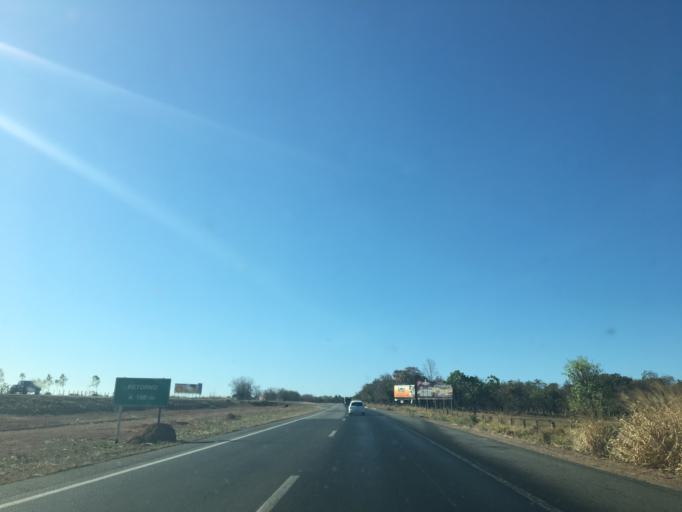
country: BR
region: Goias
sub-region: Hidrolandia
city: Hidrolandia
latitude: -17.0622
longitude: -49.2253
